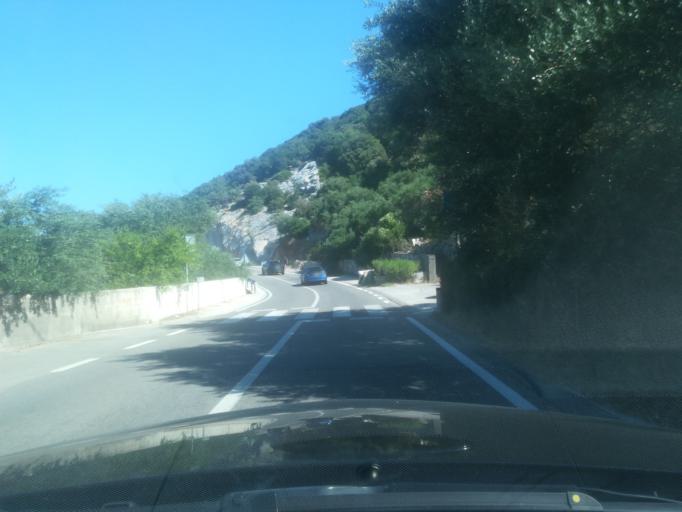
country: HR
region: Primorsko-Goranska
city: Supetarska Draga
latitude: 44.8096
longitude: 14.7187
